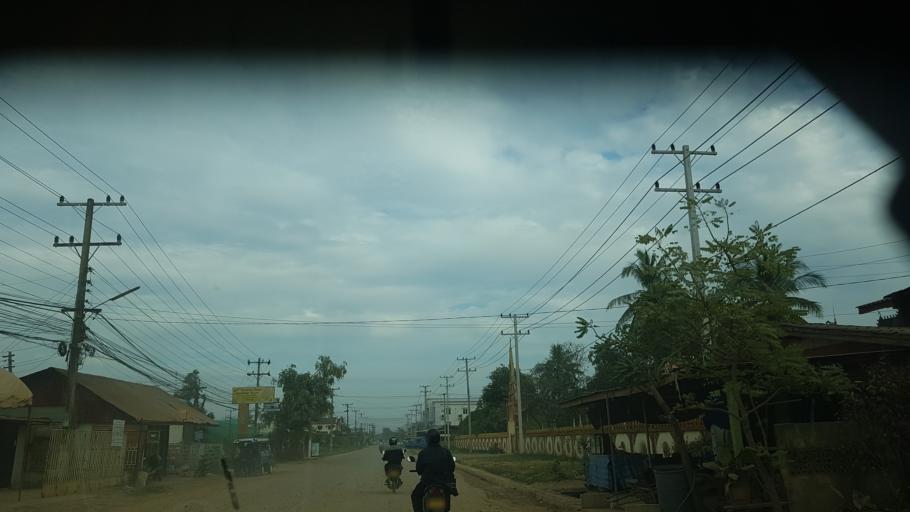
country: TH
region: Nong Khai
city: Nong Khai
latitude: 17.8870
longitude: 102.7272
